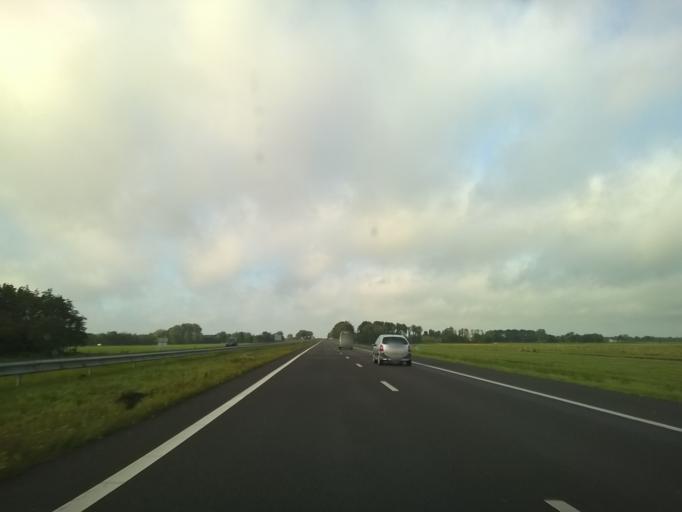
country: NL
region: Groningen
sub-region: Gemeente Grootegast
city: Grootegast
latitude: 53.1491
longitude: 6.2533
